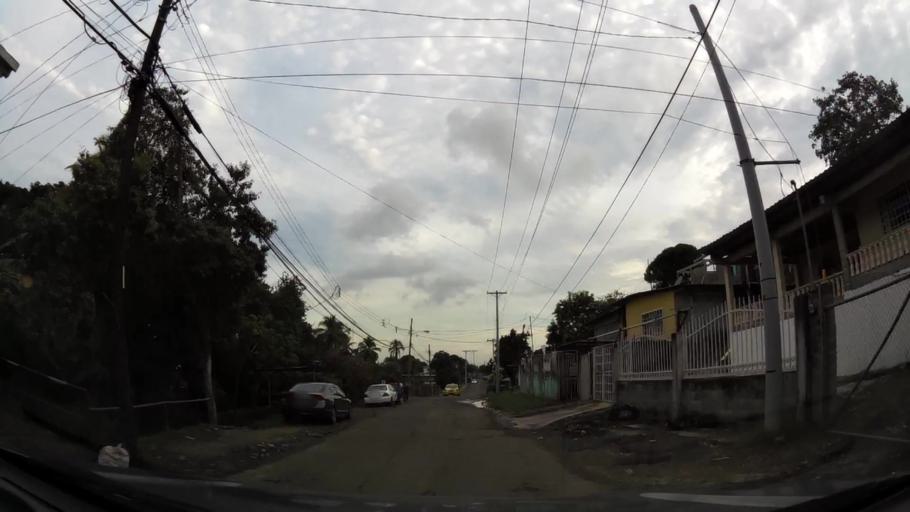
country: PA
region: Panama
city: Tocumen
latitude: 9.0872
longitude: -79.3939
